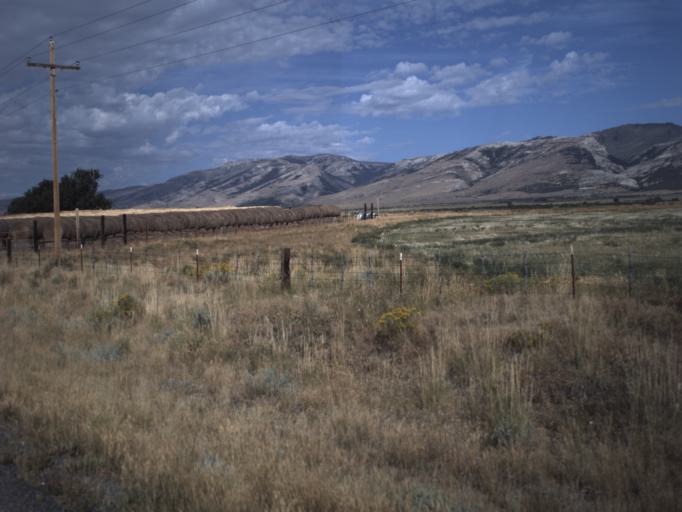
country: US
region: Idaho
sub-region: Cassia County
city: Burley
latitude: 41.8169
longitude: -113.3402
